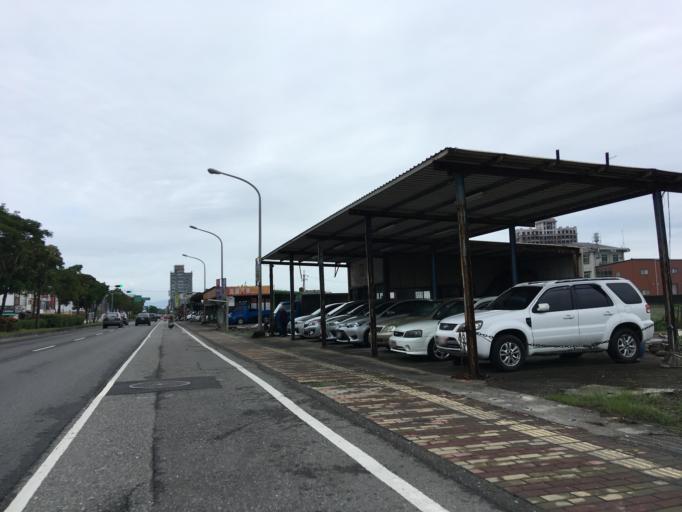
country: TW
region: Taiwan
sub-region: Yilan
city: Yilan
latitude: 24.7028
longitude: 121.7703
